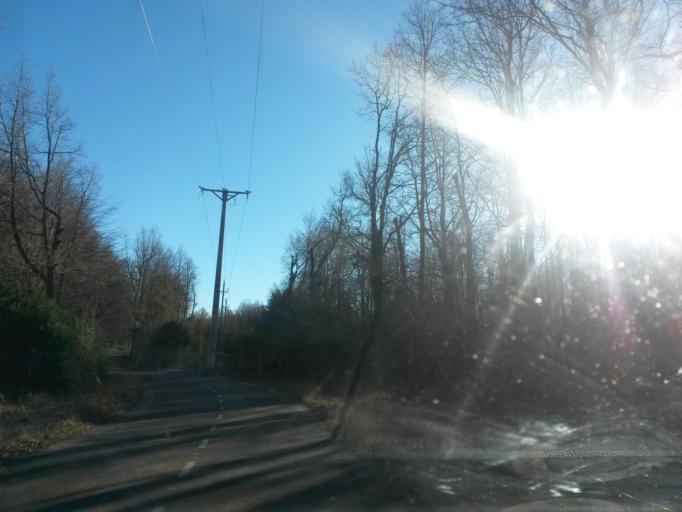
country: ES
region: Catalonia
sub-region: Provincia de Girona
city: les Planes d'Hostoles
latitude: 42.0297
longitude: 2.5256
